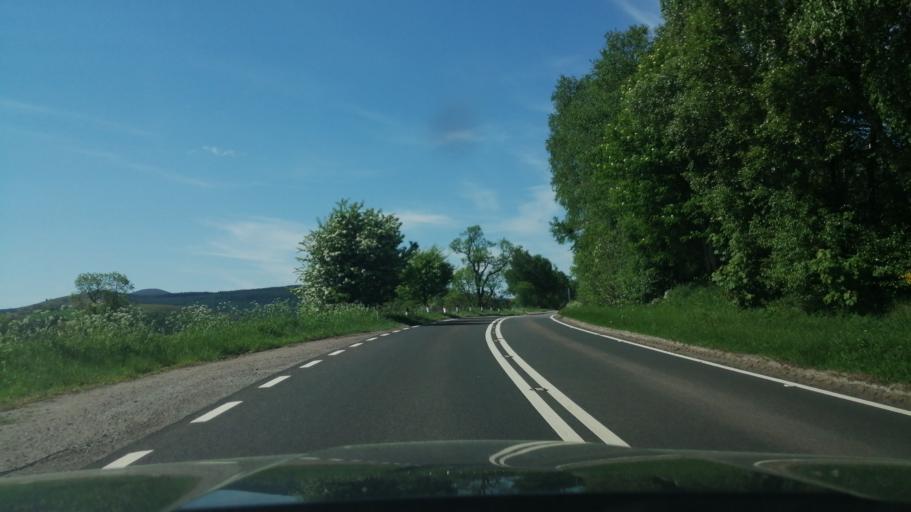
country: GB
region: Scotland
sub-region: Moray
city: Dufftown
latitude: 57.4956
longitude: -3.1470
